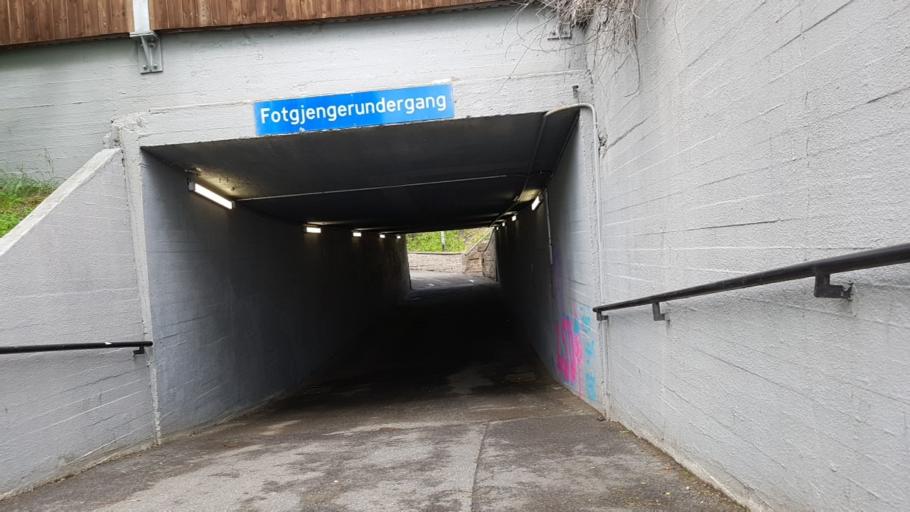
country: NO
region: Oslo
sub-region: Oslo
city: Oslo
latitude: 59.9442
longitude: 10.8188
